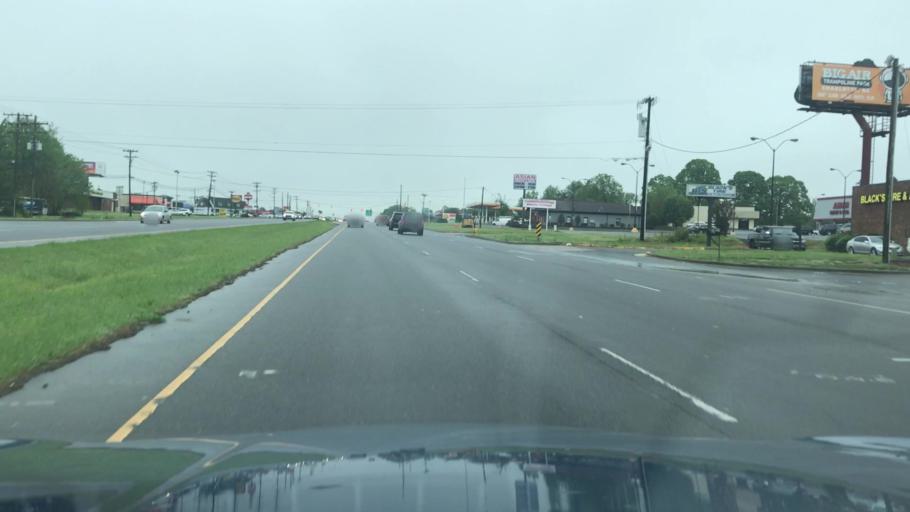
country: US
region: North Carolina
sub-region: Mecklenburg County
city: Matthews
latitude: 35.1213
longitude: -80.7006
